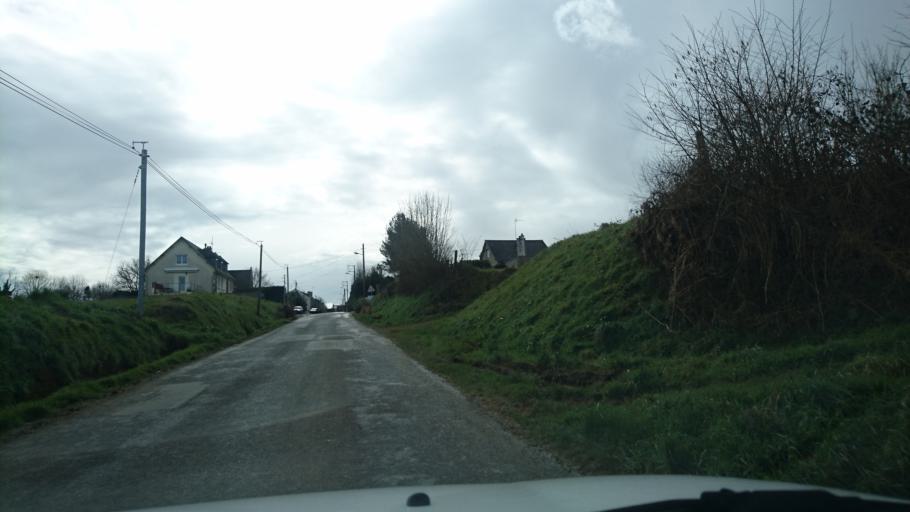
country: FR
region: Brittany
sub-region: Departement d'Ille-et-Vilaine
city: Antrain
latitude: 48.4645
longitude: -1.4880
